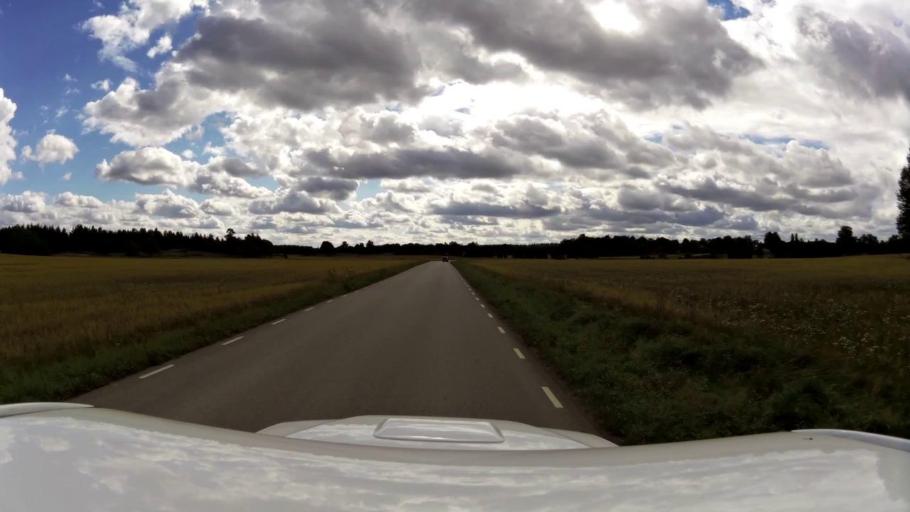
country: SE
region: OEstergoetland
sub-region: Linkopings Kommun
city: Linkoping
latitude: 58.3781
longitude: 15.5944
